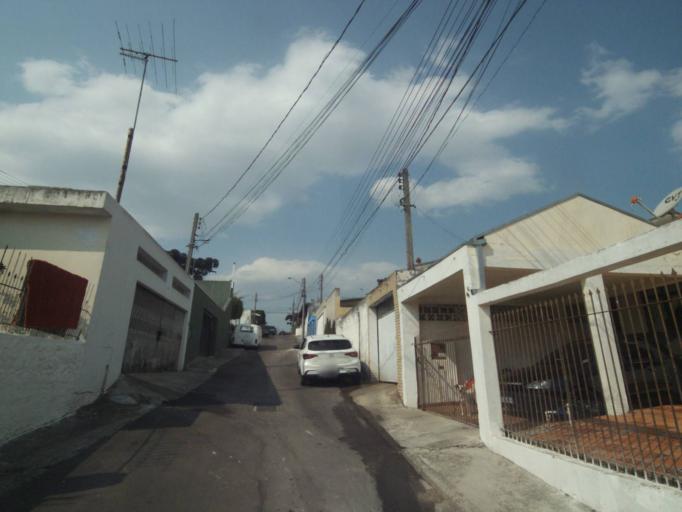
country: BR
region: Parana
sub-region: Sao Jose Dos Pinhais
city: Sao Jose dos Pinhais
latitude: -25.5224
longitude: -49.2457
